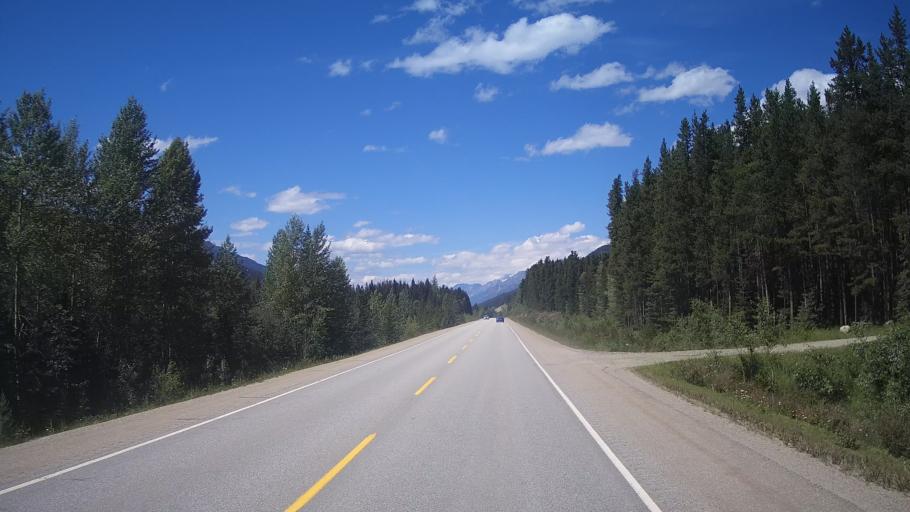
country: CA
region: Alberta
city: Jasper Park Lodge
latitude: 52.8697
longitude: -118.6786
